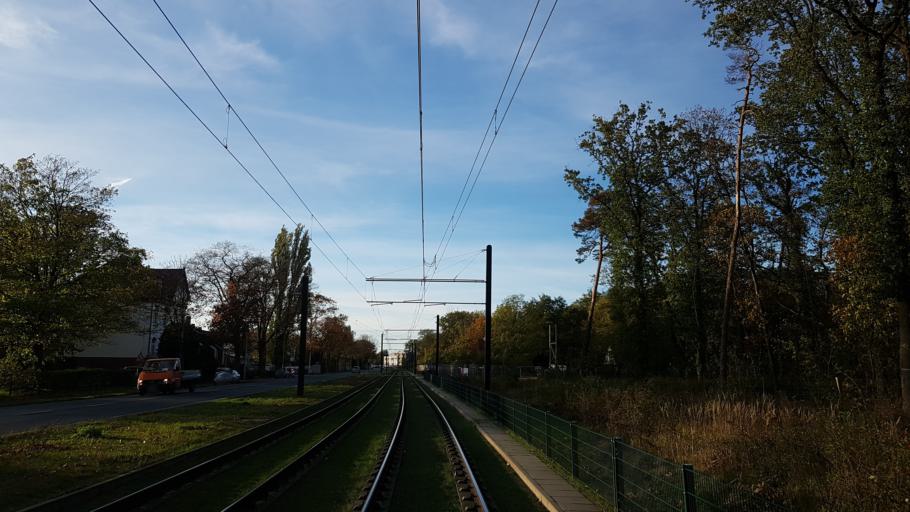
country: DE
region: Lower Saxony
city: Isernhagen Farster Bauerschaft
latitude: 52.3963
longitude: 9.8393
